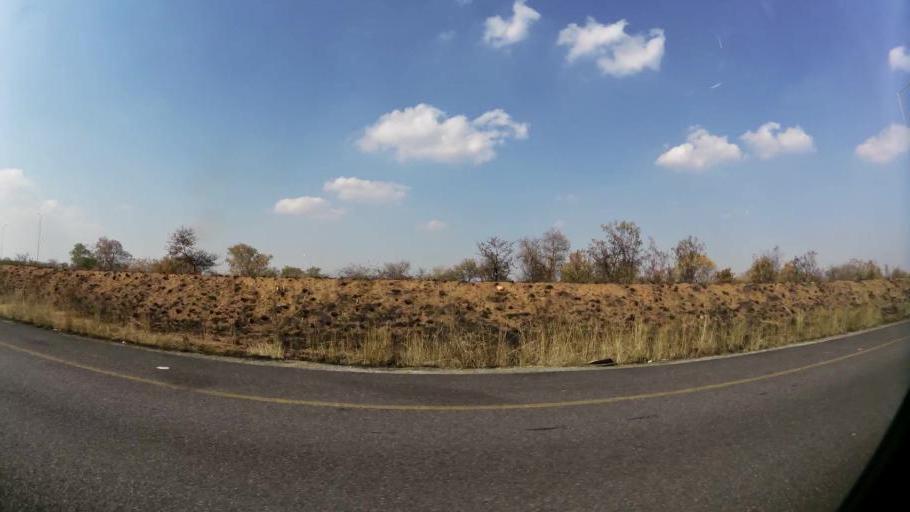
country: ZA
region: North-West
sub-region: Bojanala Platinum District Municipality
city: Rustenburg
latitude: -25.5616
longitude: 27.1441
